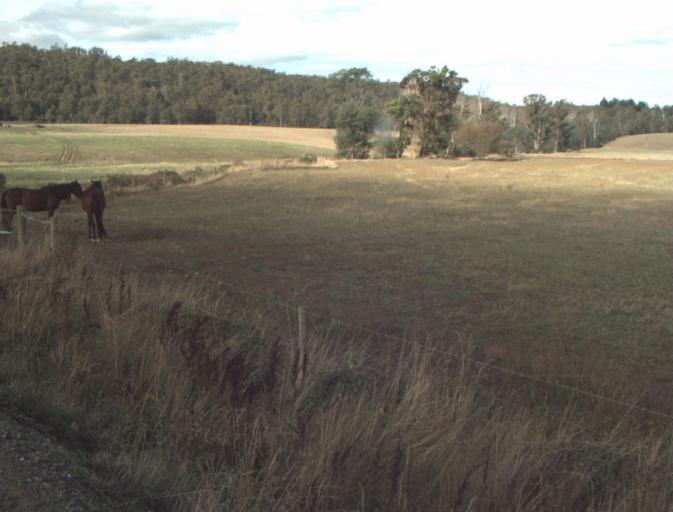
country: AU
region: Tasmania
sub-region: Launceston
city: Mayfield
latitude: -41.2128
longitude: 147.1488
